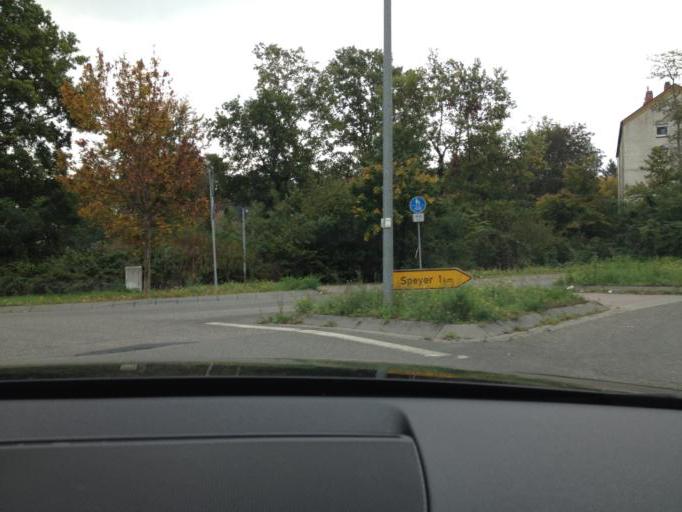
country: DE
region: Rheinland-Pfalz
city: Speyer
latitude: 49.3458
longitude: 8.4210
